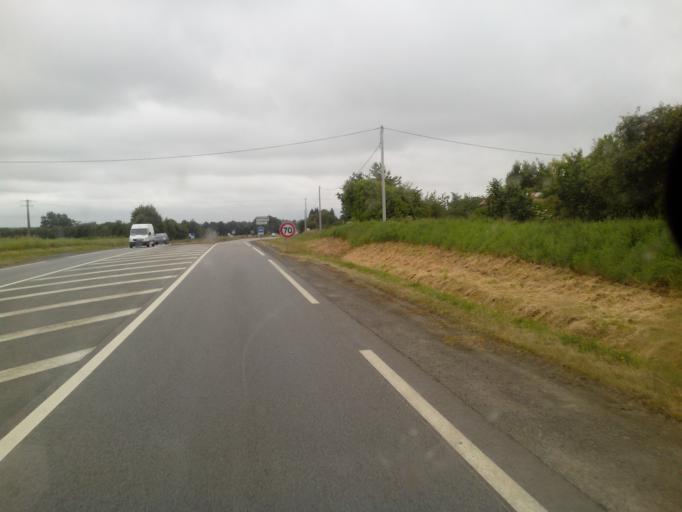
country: FR
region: Brittany
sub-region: Departement d'Ille-et-Vilaine
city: Chevaigne
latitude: 48.2373
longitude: -1.6220
